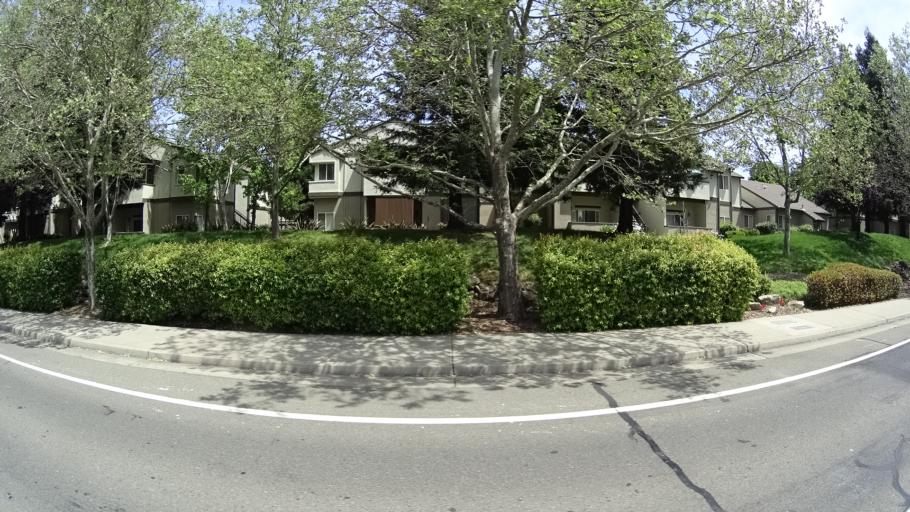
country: US
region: California
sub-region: Placer County
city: Rocklin
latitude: 38.8019
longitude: -121.2704
